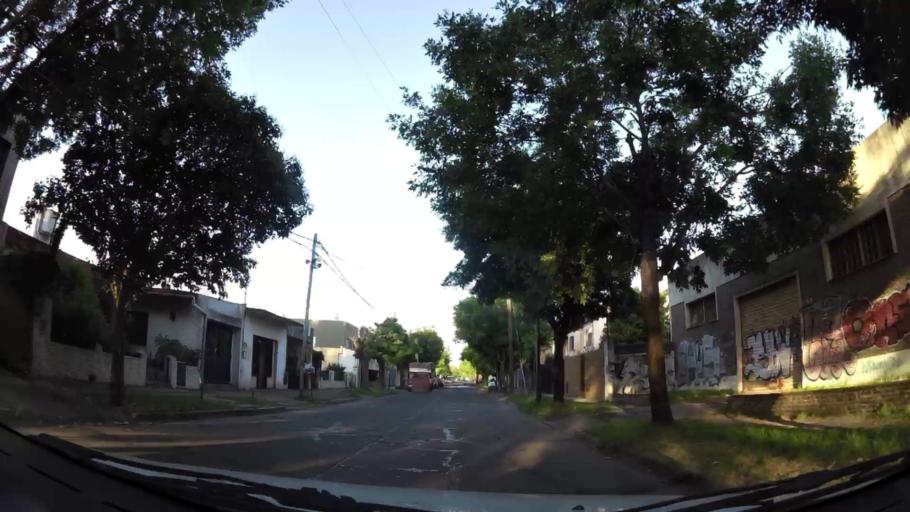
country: AR
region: Buenos Aires
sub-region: Partido de San Isidro
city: San Isidro
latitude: -34.4710
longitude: -58.5533
